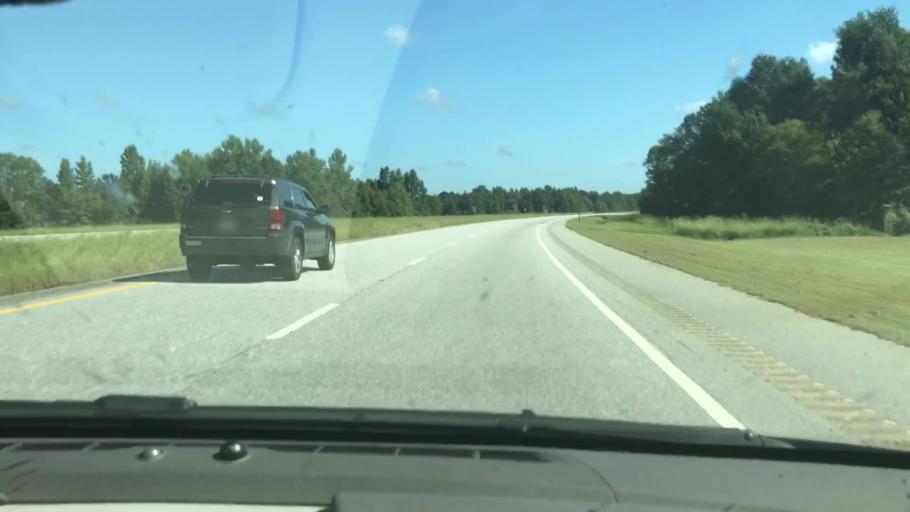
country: US
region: Alabama
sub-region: Russell County
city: Ladonia
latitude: 32.1920
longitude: -85.1812
